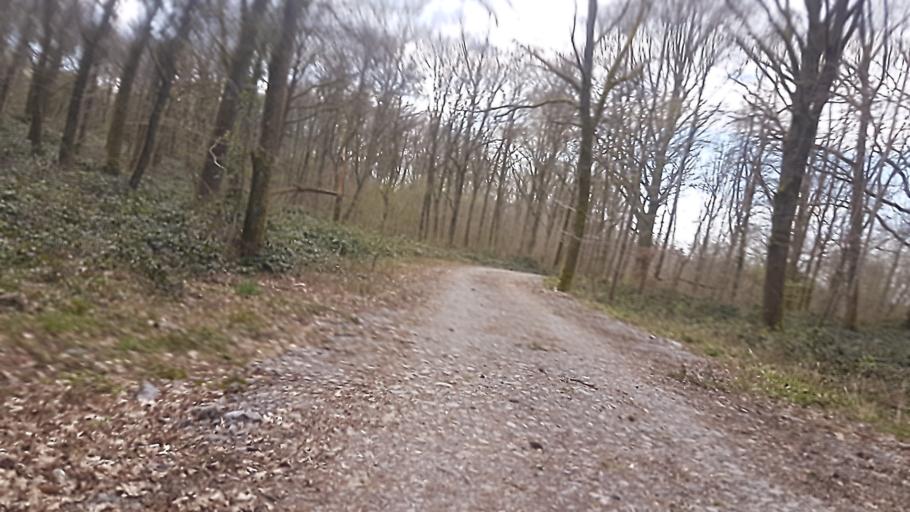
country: BE
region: Wallonia
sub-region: Province de Namur
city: Couvin
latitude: 50.0662
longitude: 4.5822
